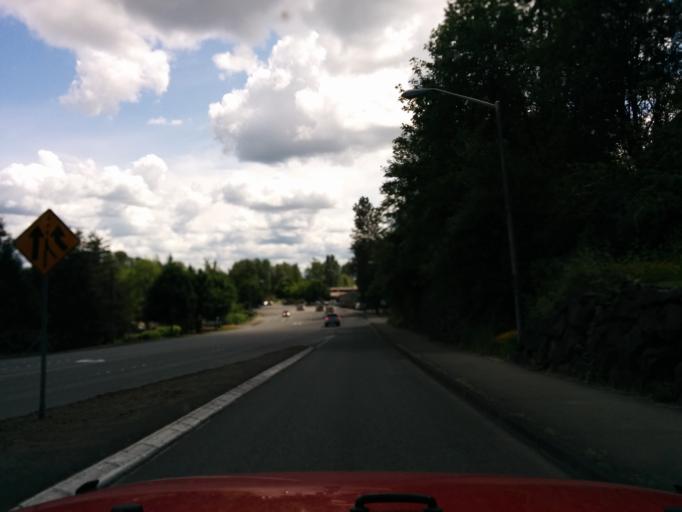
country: US
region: Washington
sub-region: King County
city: Redmond
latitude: 47.6712
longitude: -122.1325
